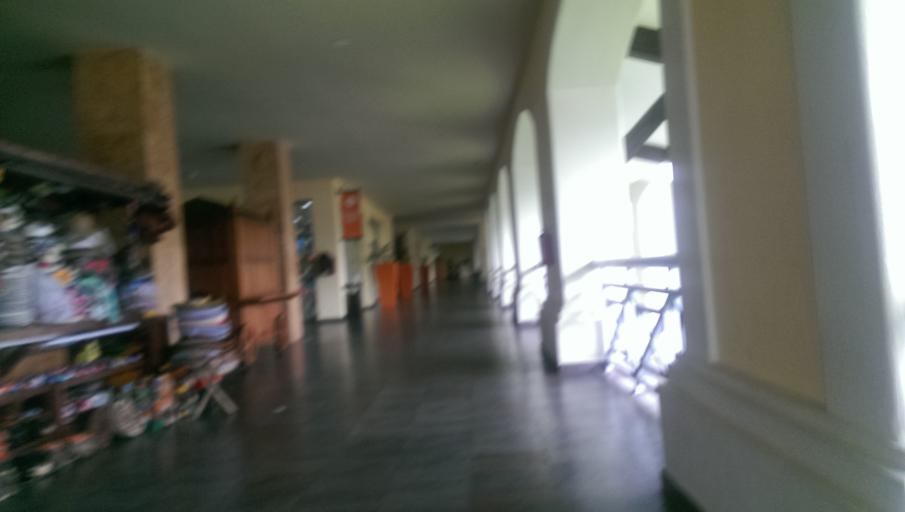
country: MX
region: Quintana Roo
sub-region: Tulum
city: Ciudad Chemuyil
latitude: 20.4897
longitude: -87.2375
